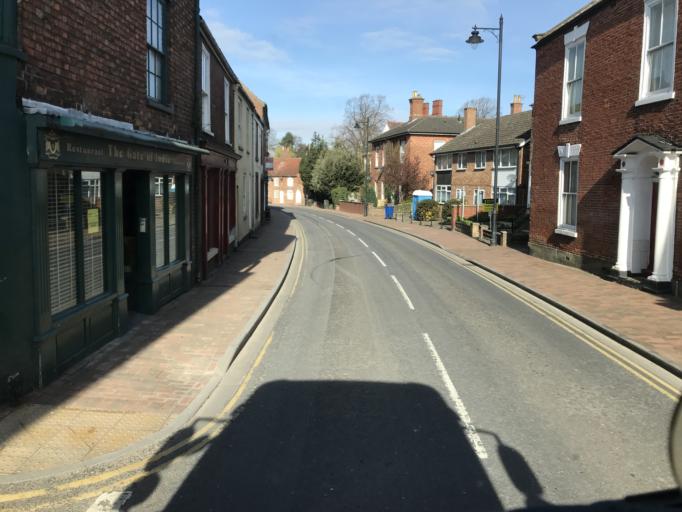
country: GB
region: England
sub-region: Lincolnshire
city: Market Rasen
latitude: 53.3880
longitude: -0.3386
